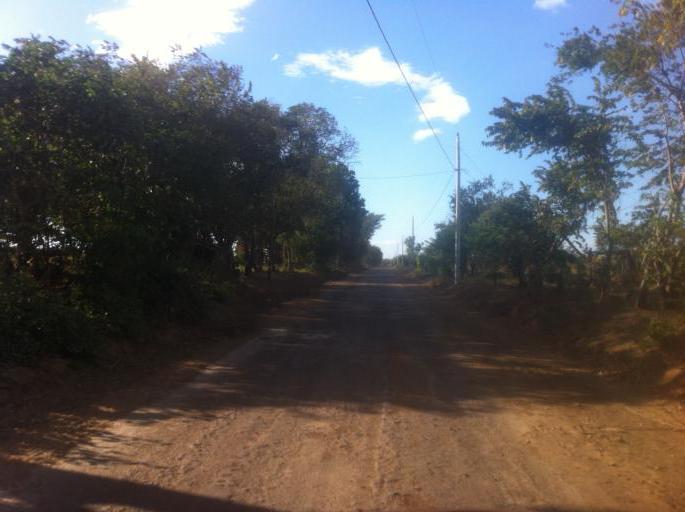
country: NI
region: Managua
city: Masachapa
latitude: 11.8441
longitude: -86.5362
